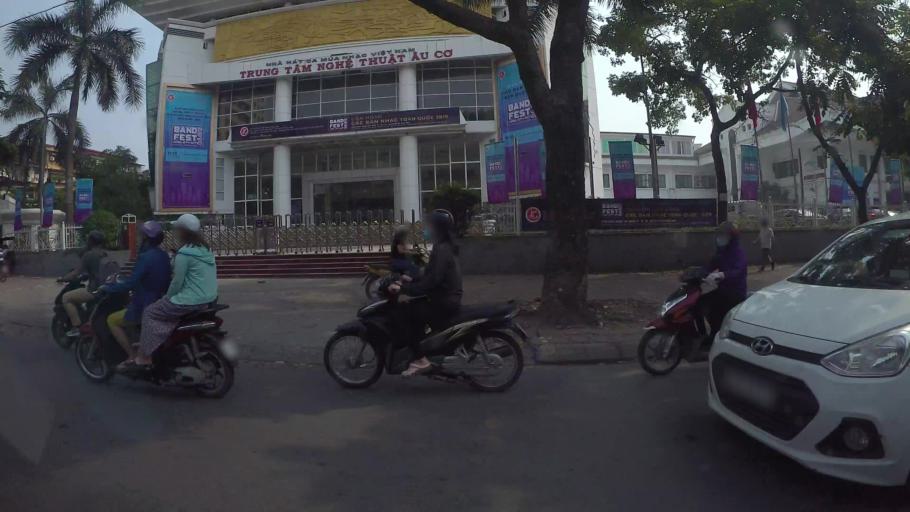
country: VN
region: Ha Noi
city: Cau Giay
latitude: 21.0179
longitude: 105.8121
